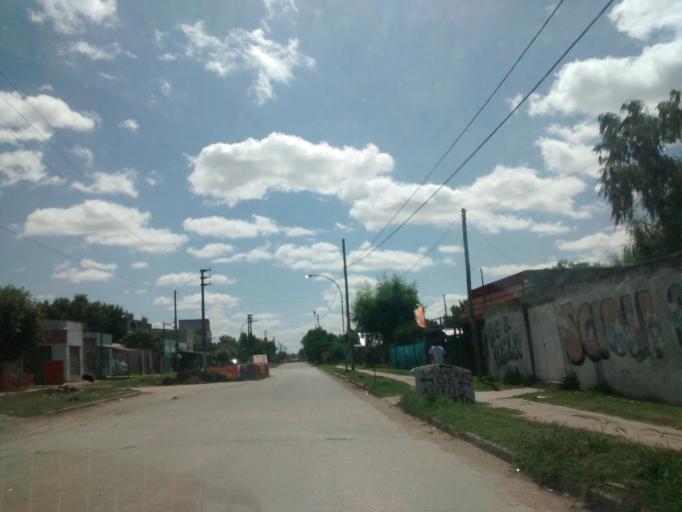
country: AR
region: Buenos Aires
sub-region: Partido de Berisso
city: Berisso
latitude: -34.8842
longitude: -57.8663
